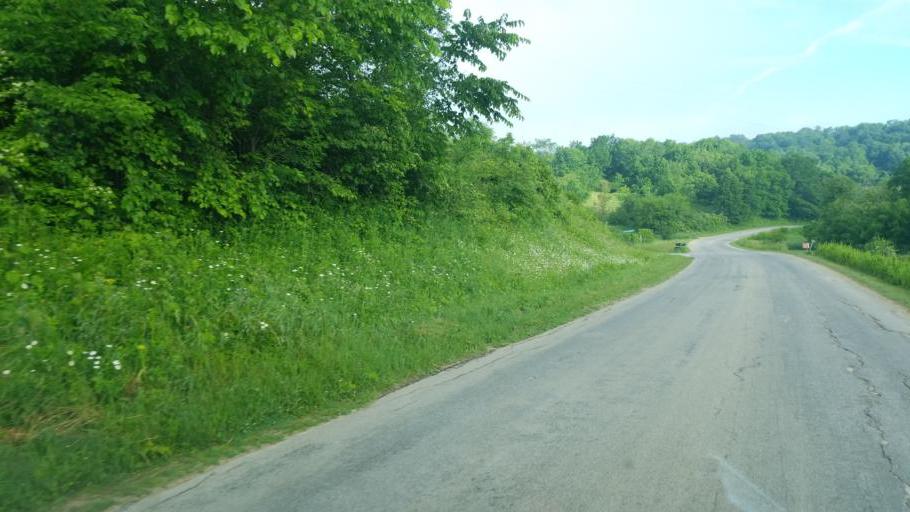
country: US
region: Wisconsin
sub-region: Vernon County
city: Hillsboro
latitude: 43.5977
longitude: -90.3680
